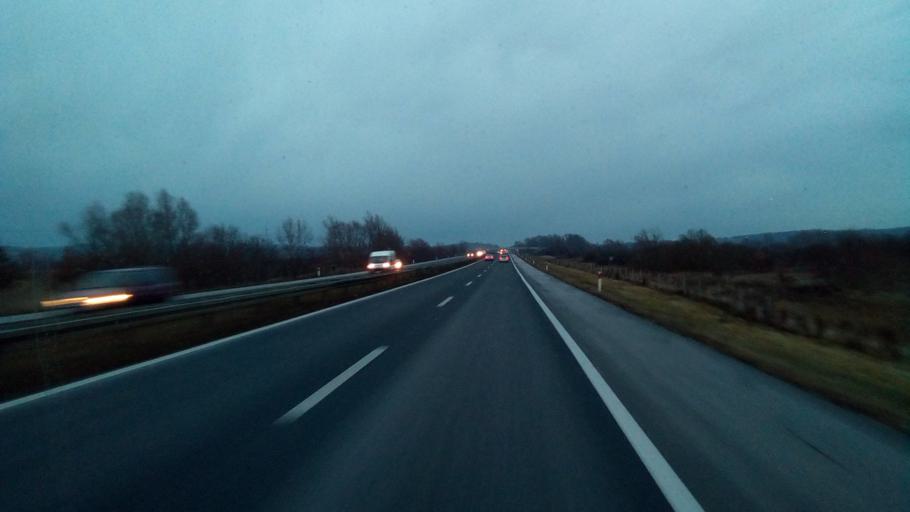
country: HR
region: Zagrebacka
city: Brckovljani
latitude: 45.8776
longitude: 16.2127
